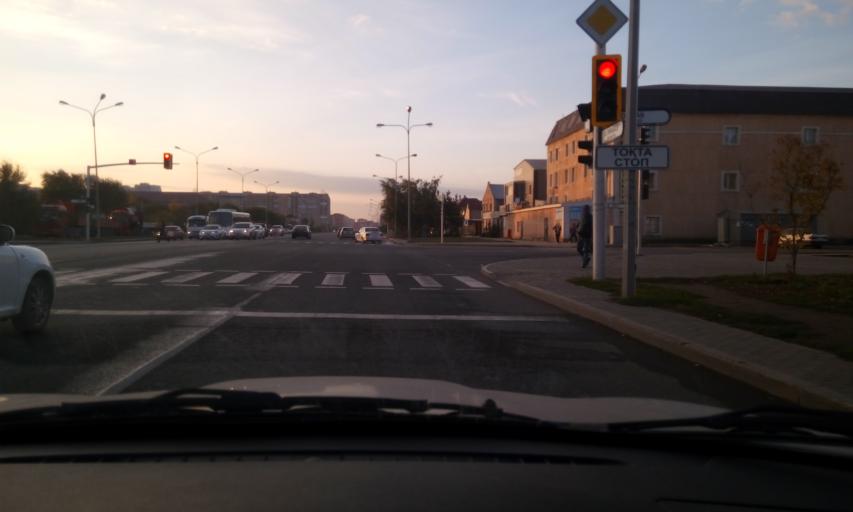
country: KZ
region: Astana Qalasy
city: Astana
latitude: 51.1377
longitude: 71.4909
